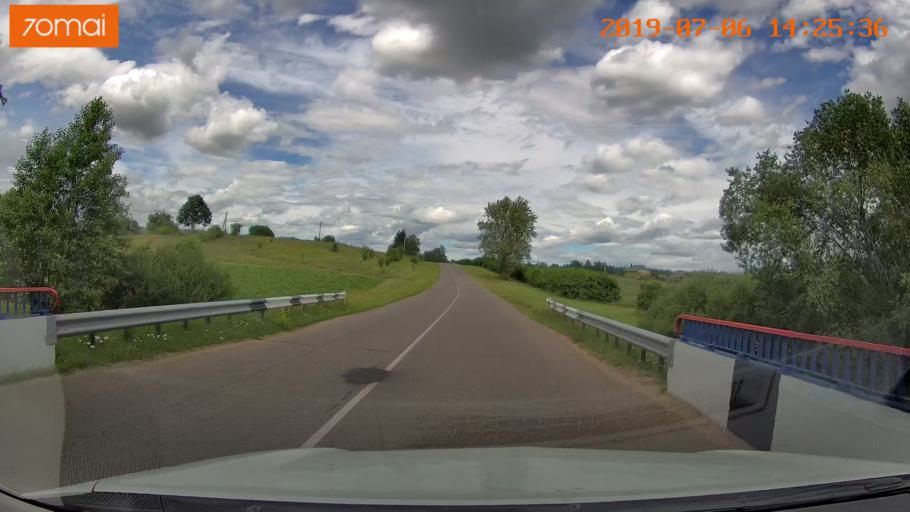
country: BY
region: Minsk
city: Ivyanyets
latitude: 53.9306
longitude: 26.7935
